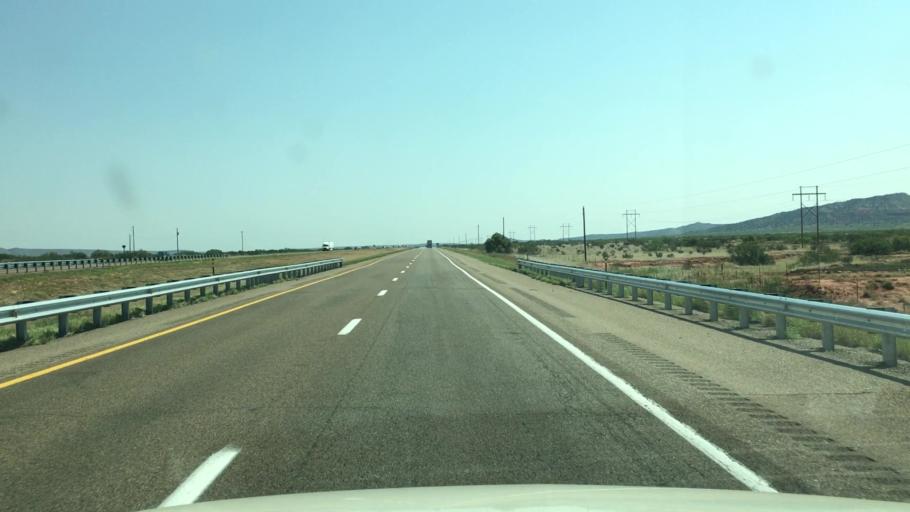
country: US
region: New Mexico
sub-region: Quay County
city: Tucumcari
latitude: 35.1026
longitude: -104.0381
